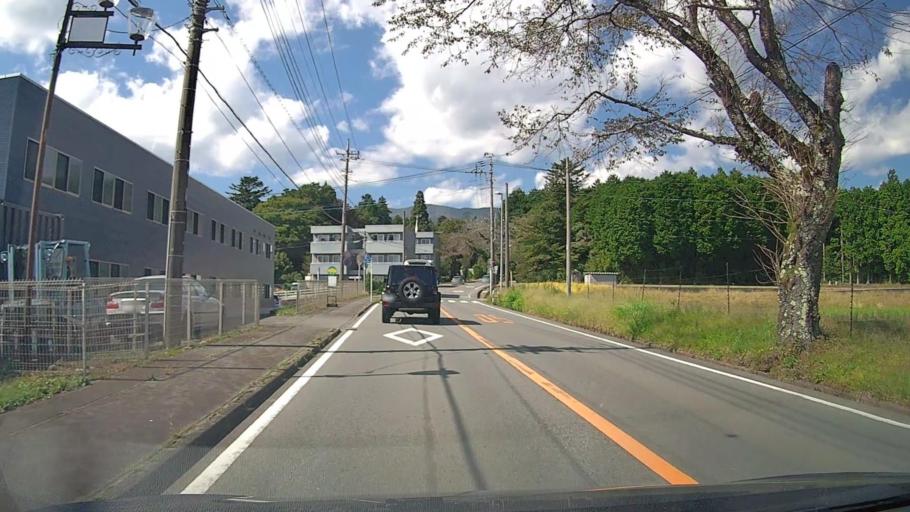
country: JP
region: Shizuoka
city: Gotemba
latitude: 35.3520
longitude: 138.9394
